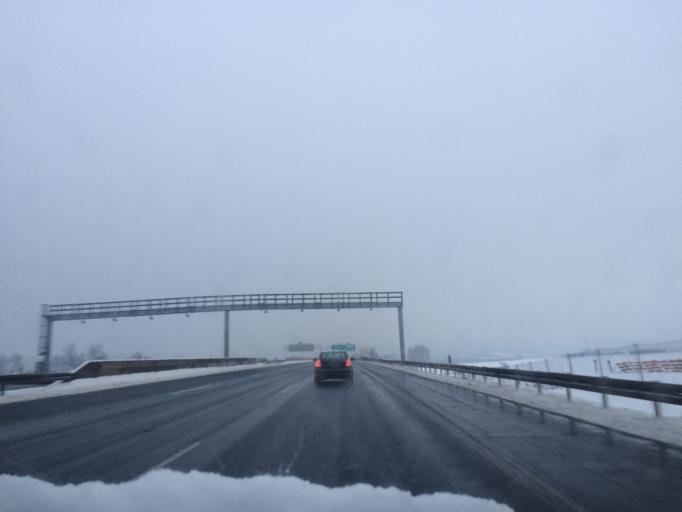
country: CZ
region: Central Bohemia
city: Hostivice
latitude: 50.0883
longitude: 14.2952
